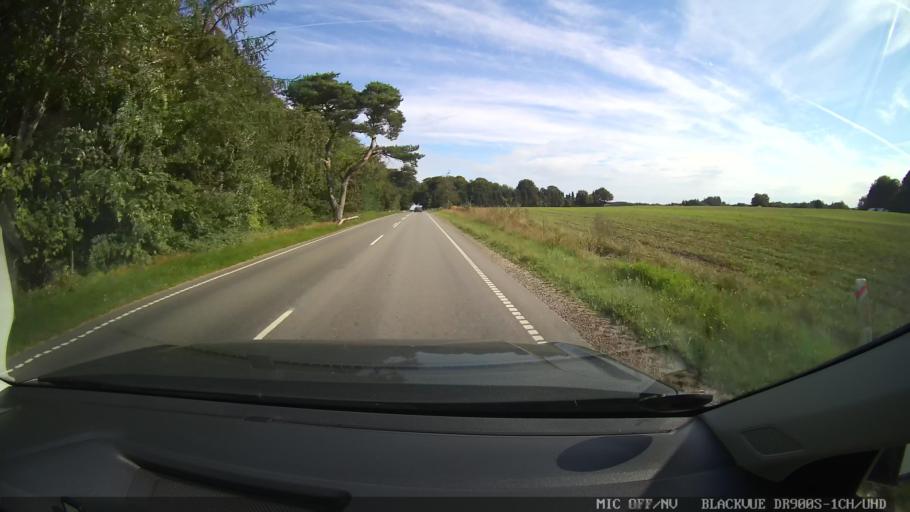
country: DK
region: North Denmark
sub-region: Mariagerfjord Kommune
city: Hadsund
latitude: 56.7903
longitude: 10.0255
